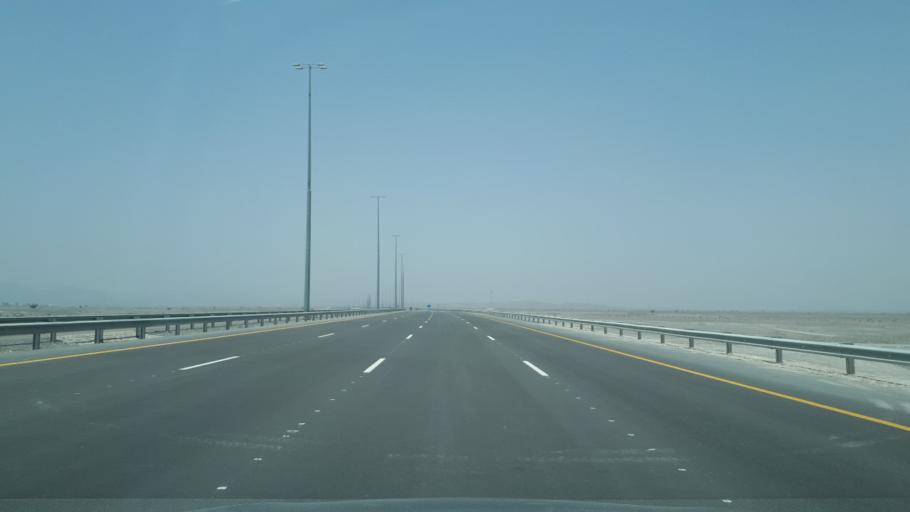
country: OM
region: Al Batinah
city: Barka'
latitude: 23.5645
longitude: 57.7022
